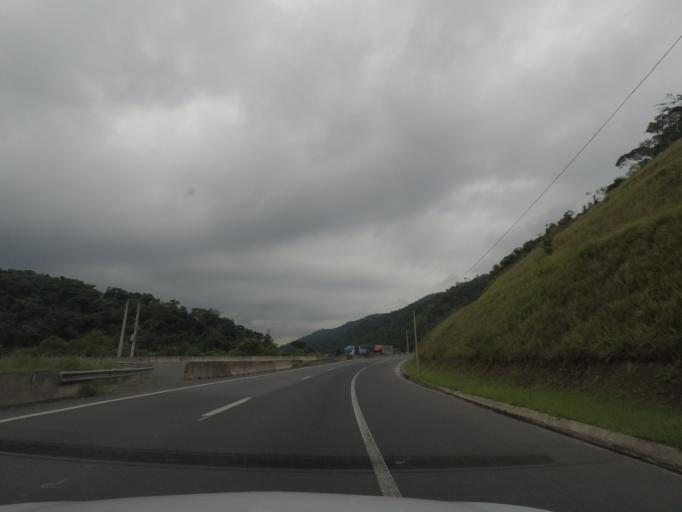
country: BR
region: Sao Paulo
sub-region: Miracatu
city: Miracatu
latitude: -24.1205
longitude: -47.2692
